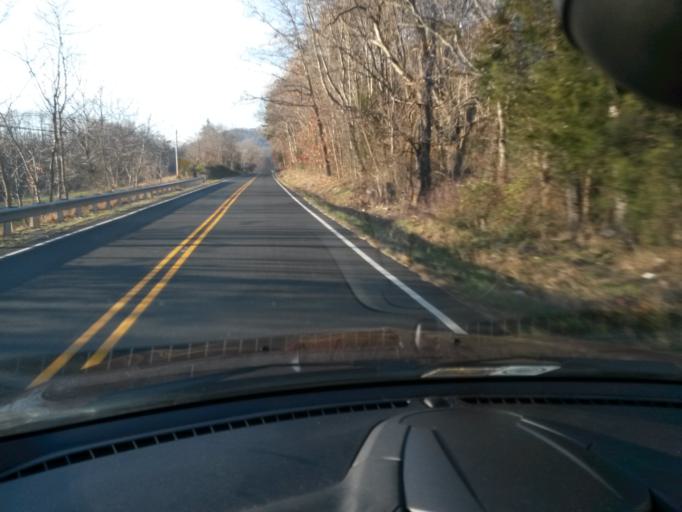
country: US
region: Virginia
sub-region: Amherst County
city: Amherst
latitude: 37.6622
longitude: -79.1584
